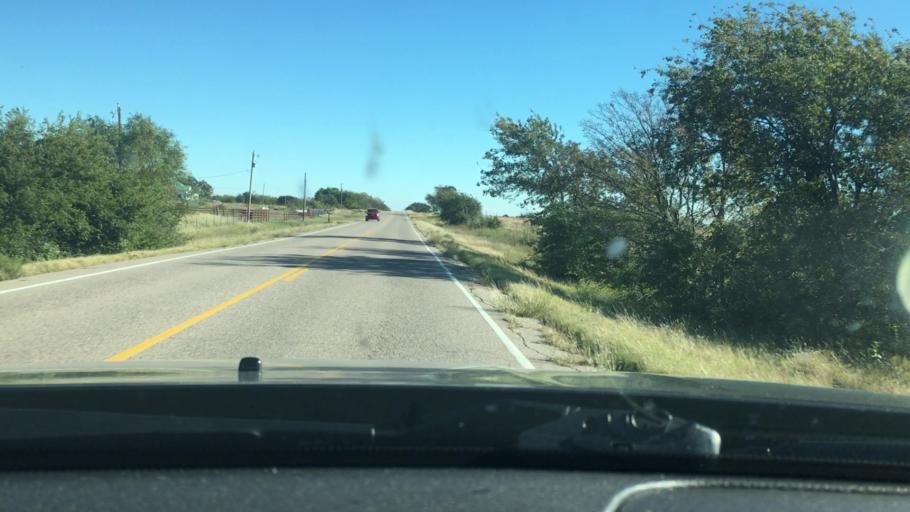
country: US
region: Oklahoma
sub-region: Marshall County
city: Madill
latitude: 34.1330
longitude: -96.7189
